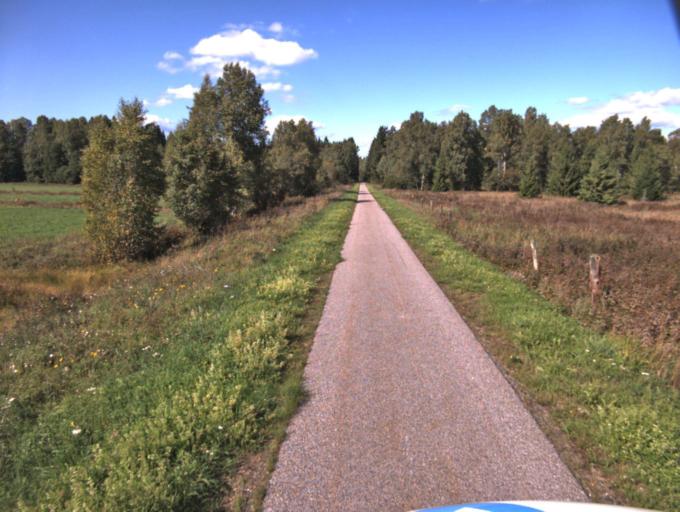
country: SE
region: Vaestra Goetaland
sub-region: Ulricehamns Kommun
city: Ulricehamn
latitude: 57.8335
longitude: 13.3401
